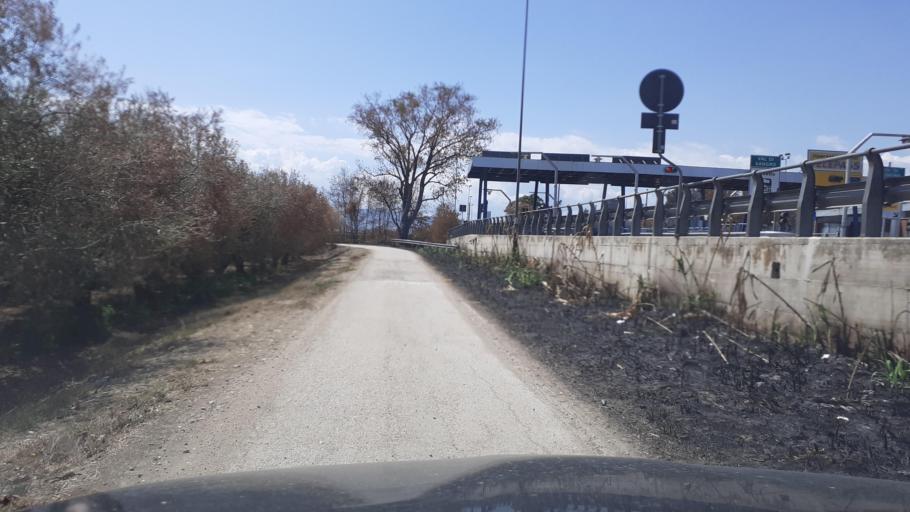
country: IT
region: Abruzzo
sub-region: Provincia di Chieti
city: Fossacesia
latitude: 42.2134
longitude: 14.4955
